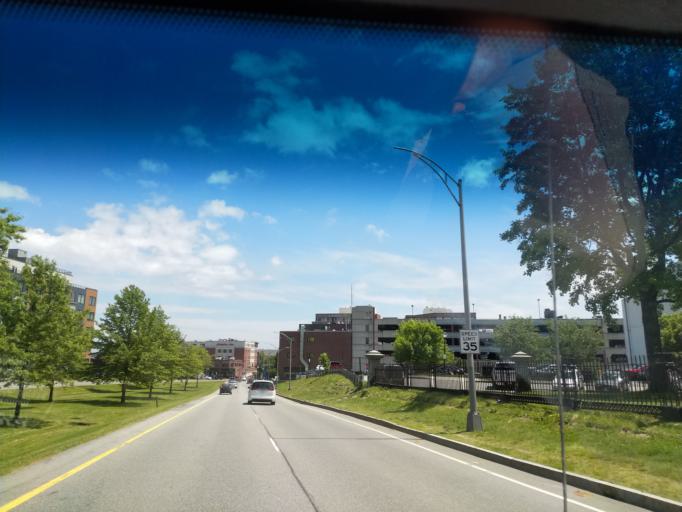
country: US
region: Maine
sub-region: Cumberland County
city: Portland
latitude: 43.6603
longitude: -70.2542
